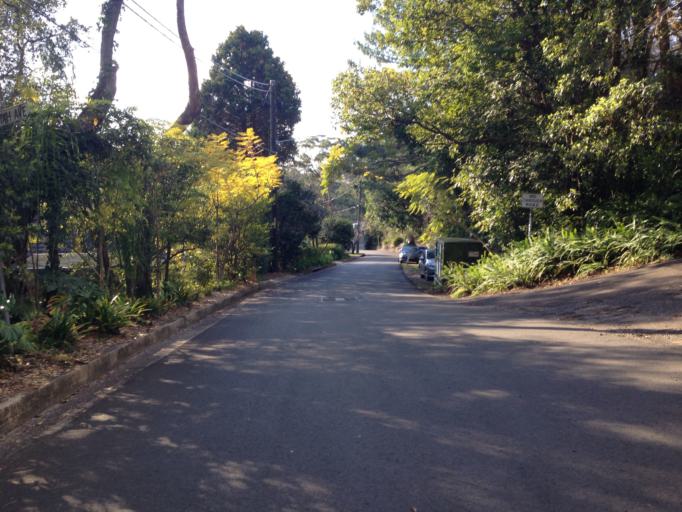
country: AU
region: New South Wales
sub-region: Ku-ring-gai
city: Killara
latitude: -33.7588
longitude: 151.1666
